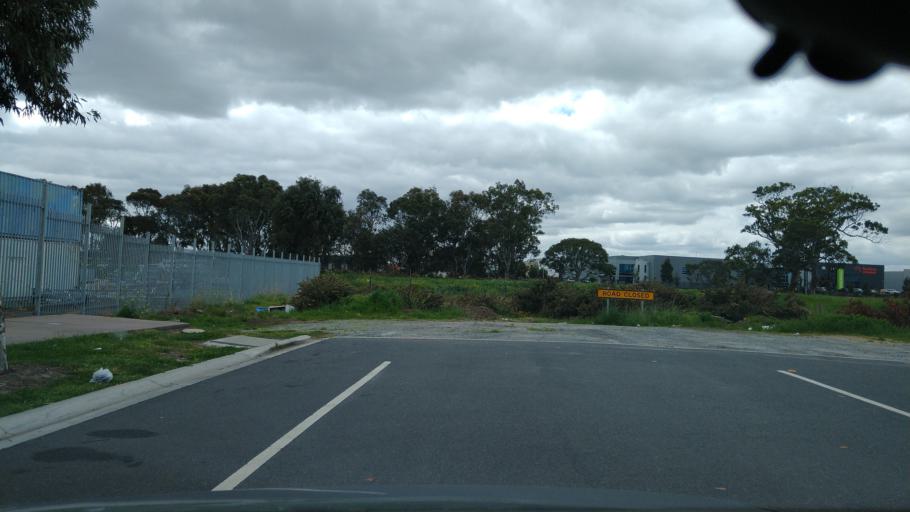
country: AU
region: Victoria
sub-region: Frankston
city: Sandhurst
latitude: -38.0475
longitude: 145.2171
